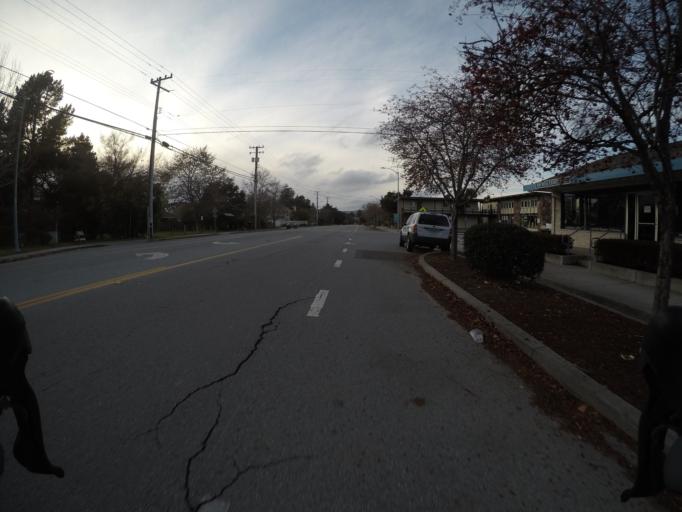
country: US
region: California
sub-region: Santa Cruz County
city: Live Oak
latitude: 36.9765
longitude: -121.9850
